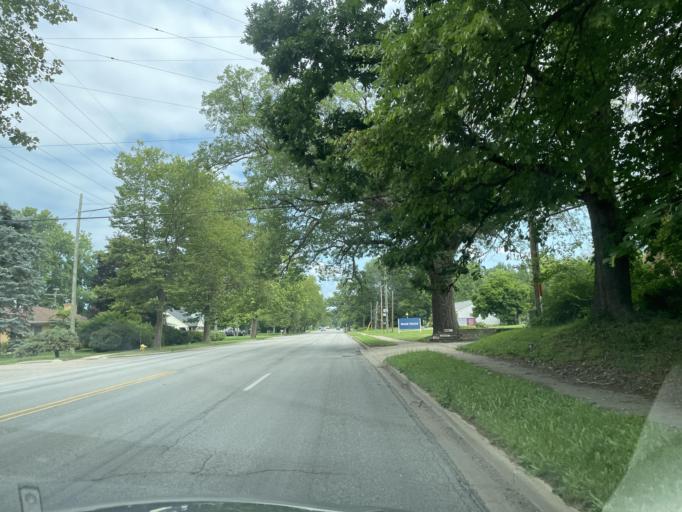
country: US
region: Michigan
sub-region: Kent County
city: Kentwood
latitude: 42.8902
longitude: -85.6262
